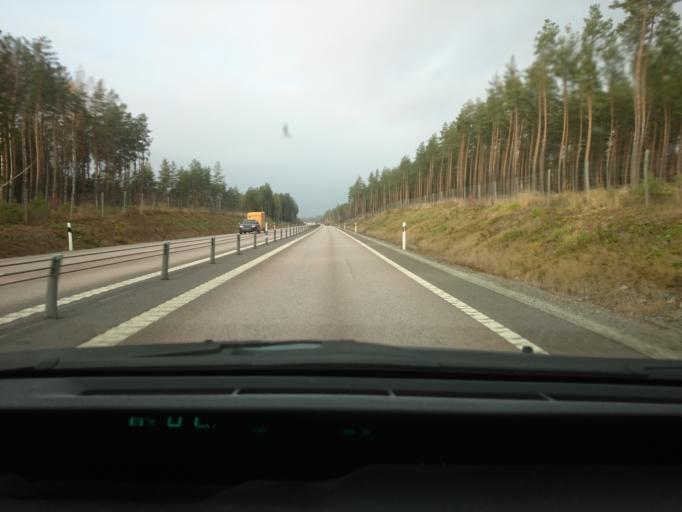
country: SE
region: Vaestmanland
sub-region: Sala Kommun
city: Sala
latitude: 59.9339
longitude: 16.5184
